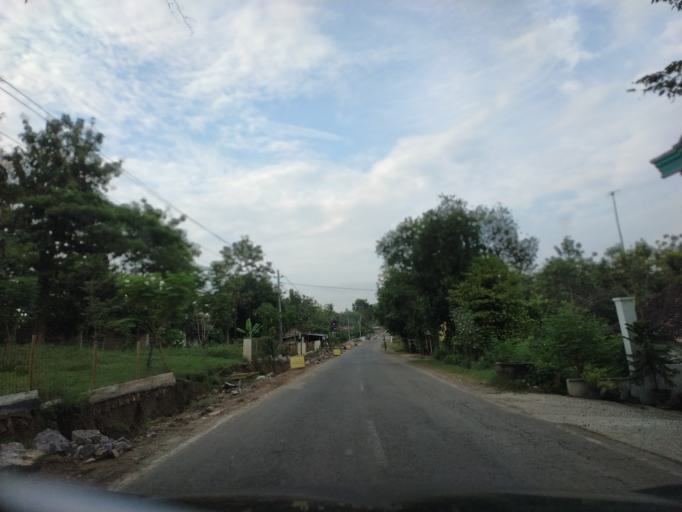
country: ID
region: Central Java
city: Medang
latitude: -6.9071
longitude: 111.4408
